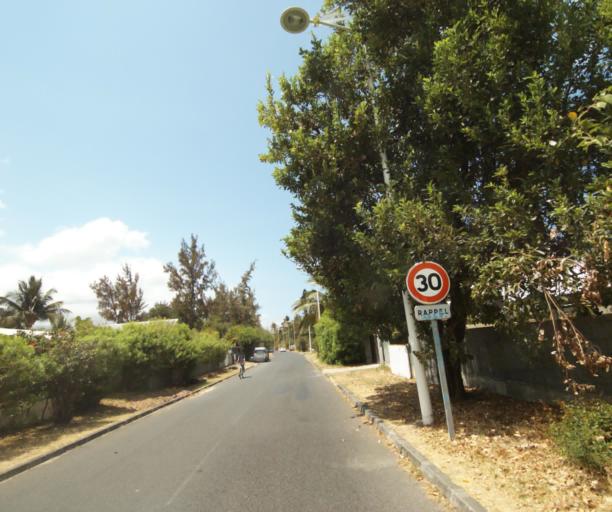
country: RE
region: Reunion
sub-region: Reunion
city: Trois-Bassins
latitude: -21.0768
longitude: 55.2268
